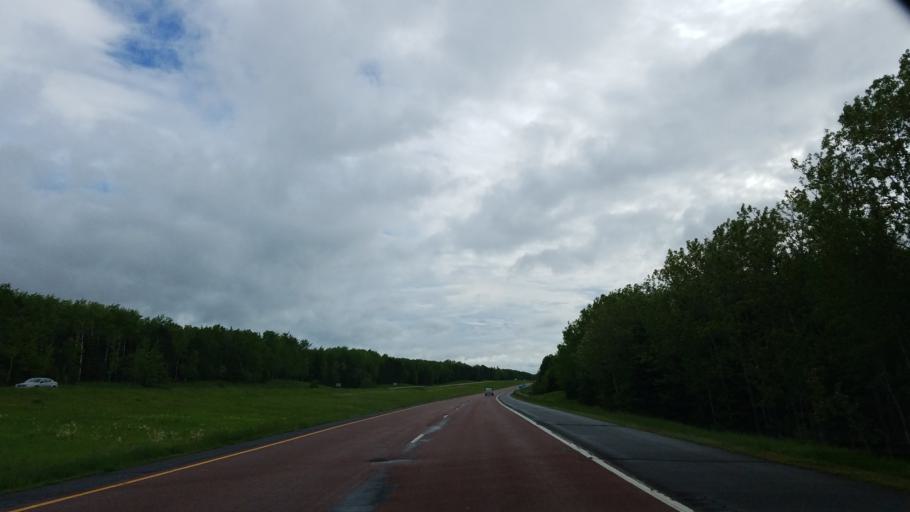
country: US
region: Minnesota
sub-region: Saint Louis County
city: Arnold
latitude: 46.9056
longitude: -91.8932
